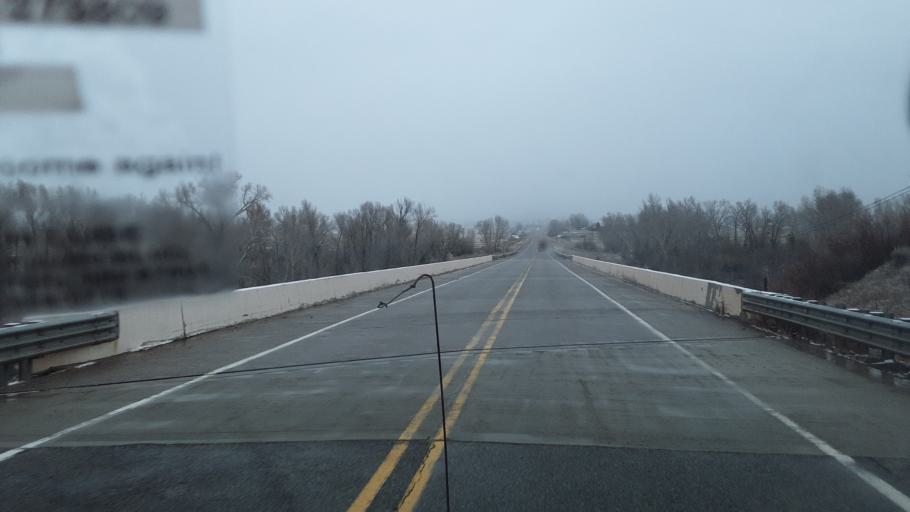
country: US
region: New Mexico
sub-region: Rio Arriba County
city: Tierra Amarilla
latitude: 36.7458
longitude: -106.5680
